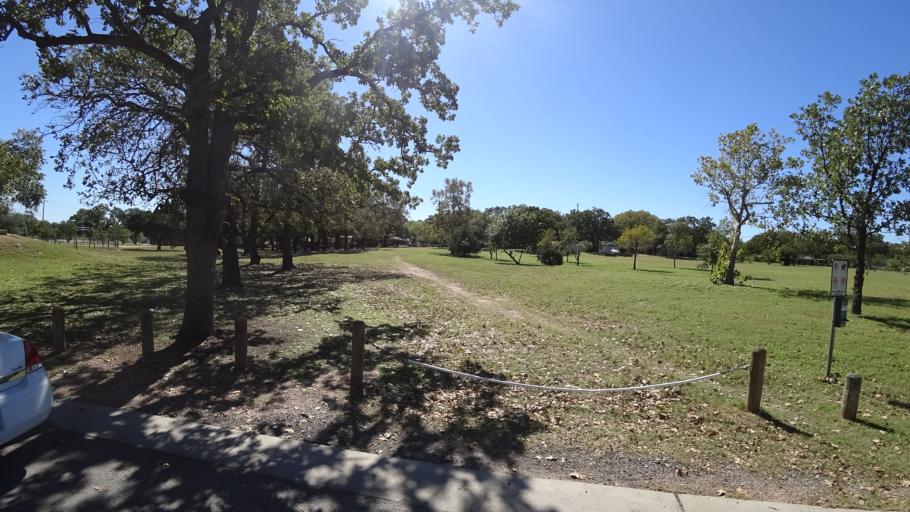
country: US
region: Texas
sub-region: Travis County
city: Austin
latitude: 30.2957
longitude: -97.7092
